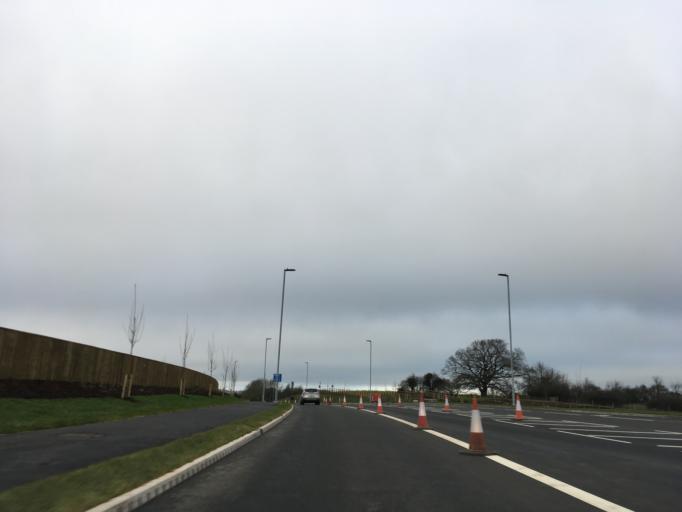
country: GB
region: England
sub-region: South Gloucestershire
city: Stoke Gifford
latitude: 51.5150
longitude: -2.5286
